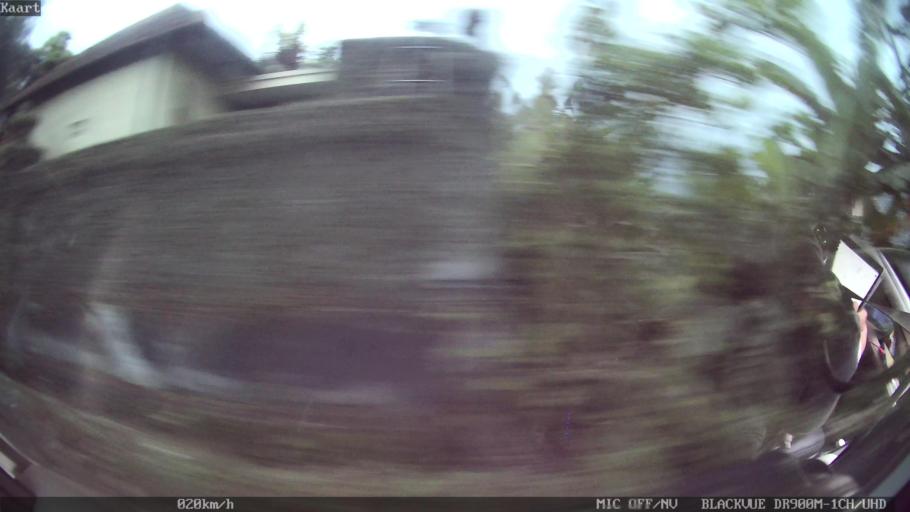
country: ID
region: Bali
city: Banjar Pasekan
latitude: -8.6147
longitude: 115.2809
